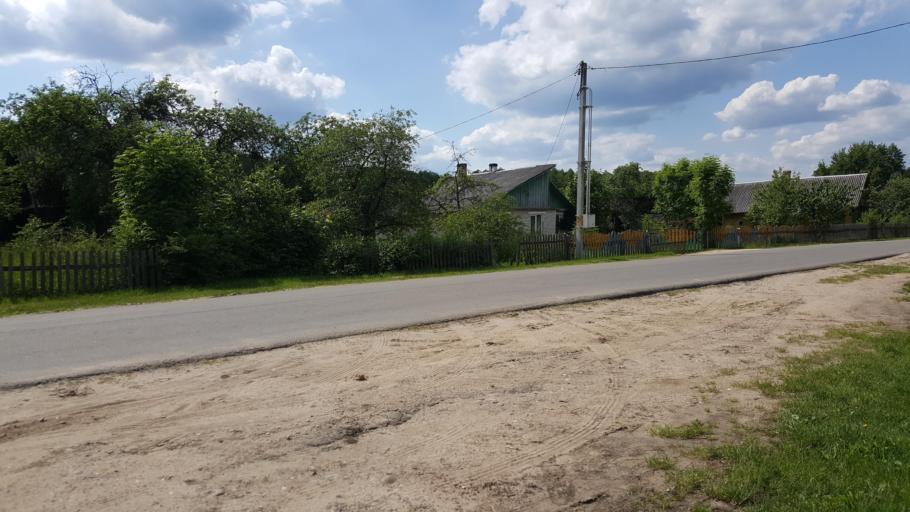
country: PL
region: Podlasie
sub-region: Powiat hajnowski
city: Bialowieza
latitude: 52.6094
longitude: 24.1106
